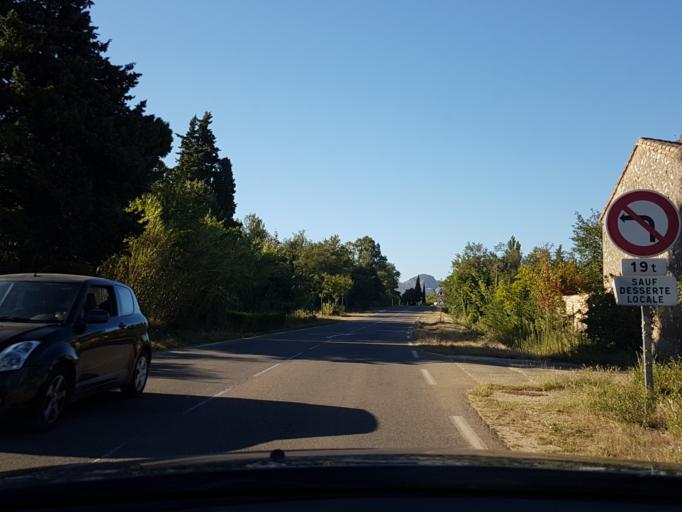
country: FR
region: Provence-Alpes-Cote d'Azur
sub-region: Departement des Bouches-du-Rhone
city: Eygalieres
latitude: 43.7747
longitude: 4.9594
